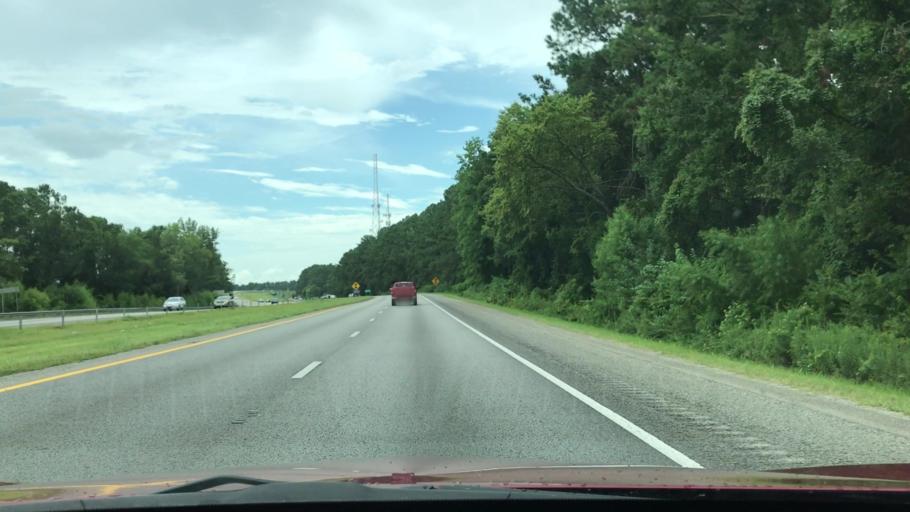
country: US
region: South Carolina
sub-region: Charleston County
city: Shell Point
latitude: 32.7988
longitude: -80.0355
